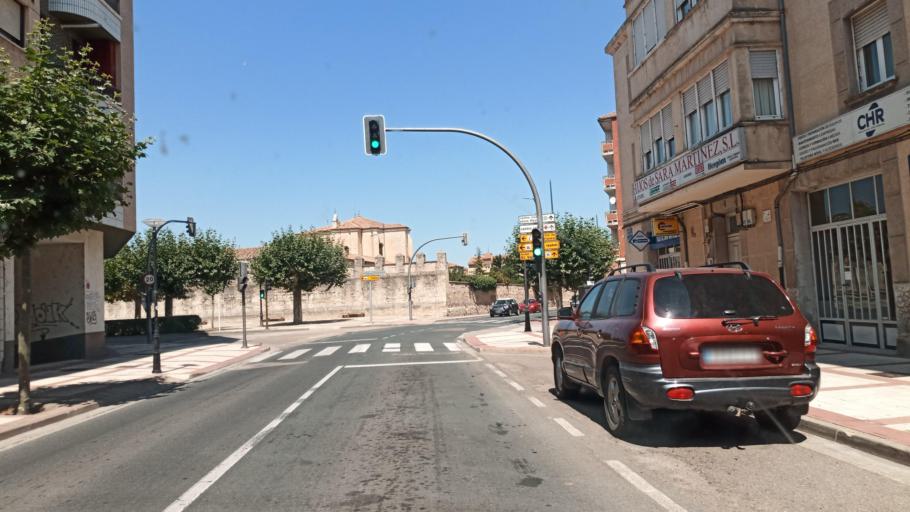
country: ES
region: Castille and Leon
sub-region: Provincia de Burgos
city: Briviesca
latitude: 42.5479
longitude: -3.3216
